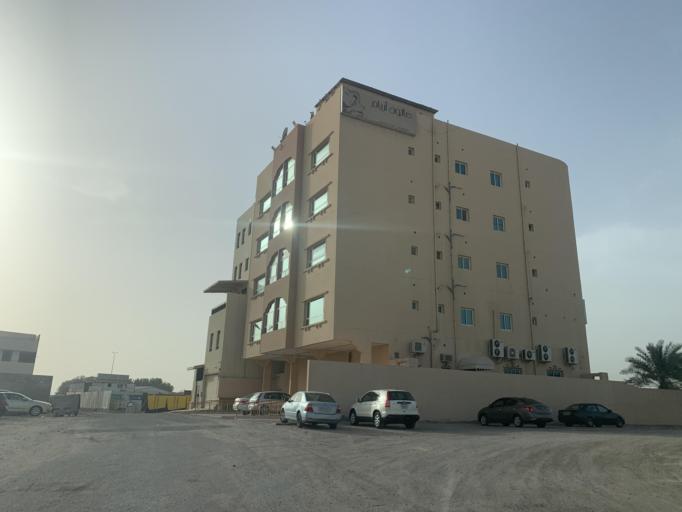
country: BH
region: Northern
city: Madinat `Isa
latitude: 26.1647
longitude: 50.5130
